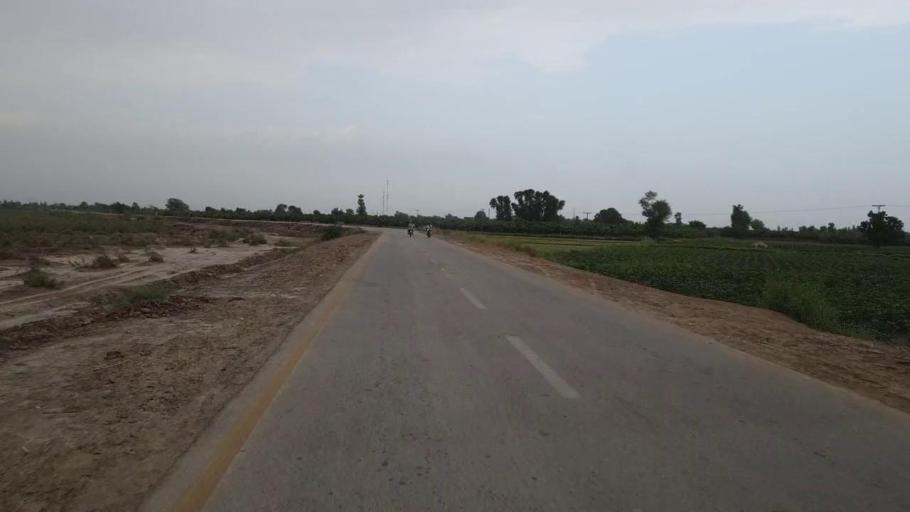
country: PK
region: Sindh
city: Bandhi
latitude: 26.5804
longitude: 68.2798
